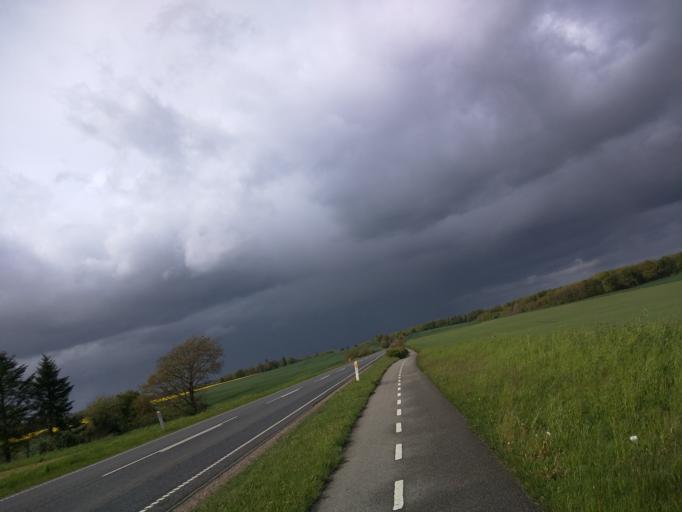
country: DK
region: Central Jutland
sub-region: Silkeborg Kommune
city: Kjellerup
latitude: 56.3075
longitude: 9.4237
